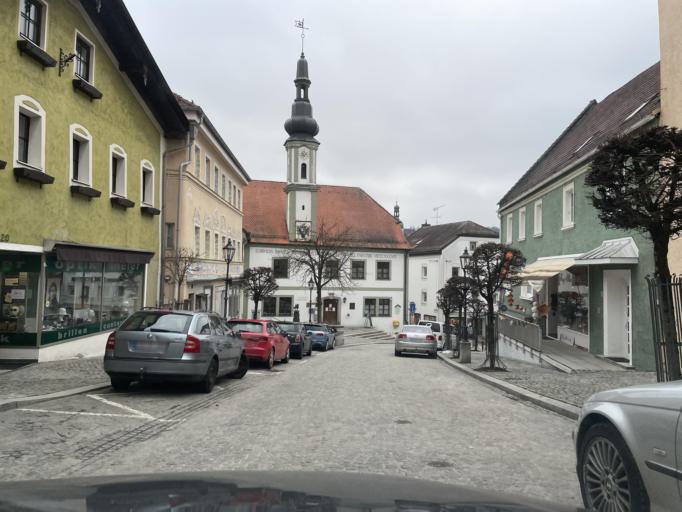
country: DE
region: Bavaria
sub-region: Upper Palatinate
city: Kotzting
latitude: 49.1762
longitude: 12.8562
